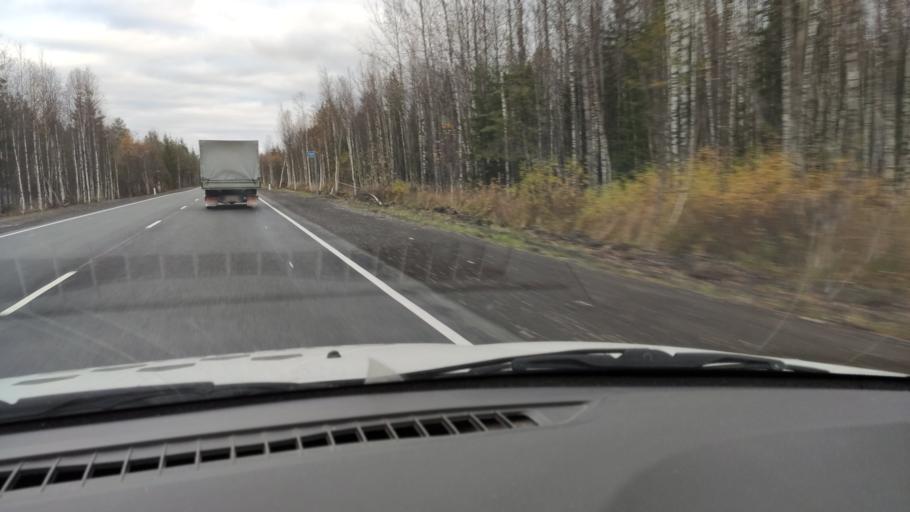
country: RU
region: Kirov
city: Chernaya Kholunitsa
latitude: 58.8741
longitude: 51.4997
